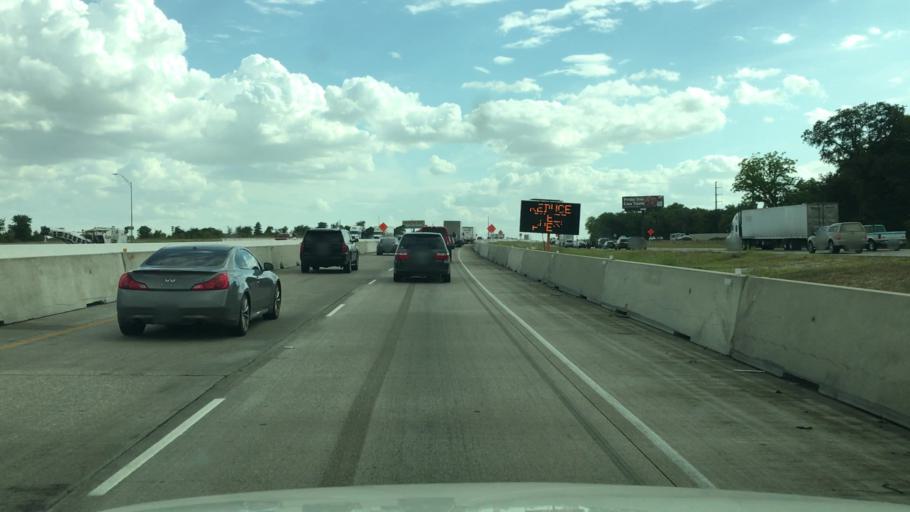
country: US
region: Texas
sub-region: McLennan County
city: Bruceville-Eddy
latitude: 31.3280
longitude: -97.2279
